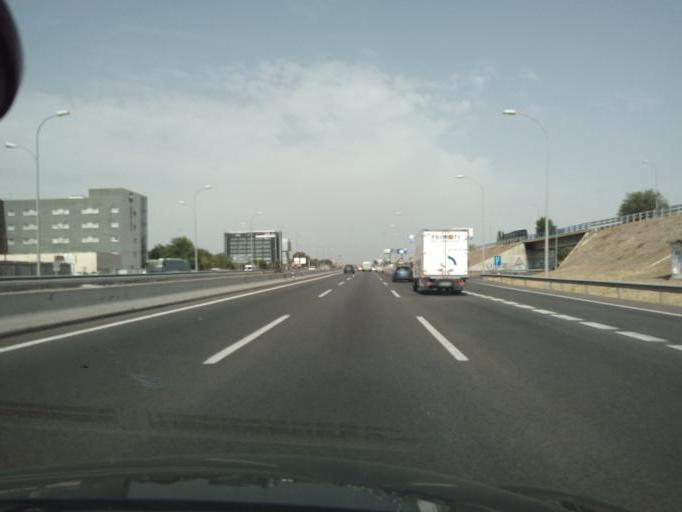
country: ES
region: Madrid
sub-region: Provincia de Madrid
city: San Fernando de Henares
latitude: 40.4478
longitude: -3.5414
